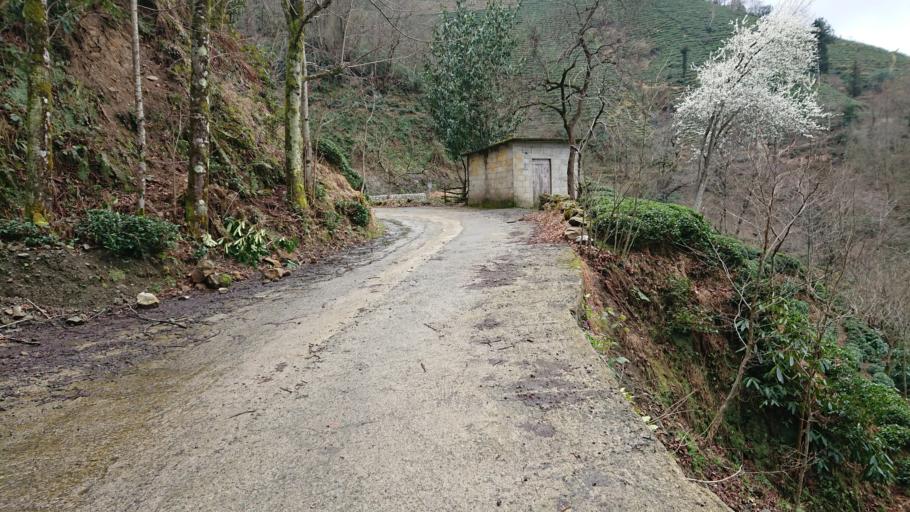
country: TR
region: Rize
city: Rize
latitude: 40.9775
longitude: 40.4964
